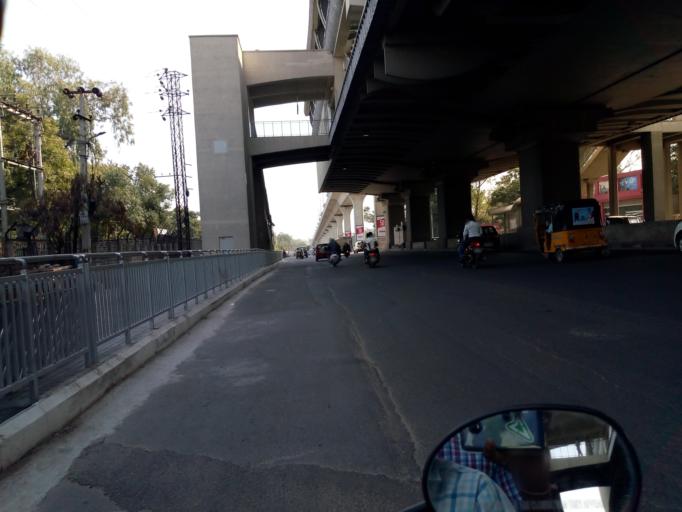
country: IN
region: Telangana
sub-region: Rangareddi
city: Uppal Kalan
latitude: 17.4149
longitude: 78.5463
